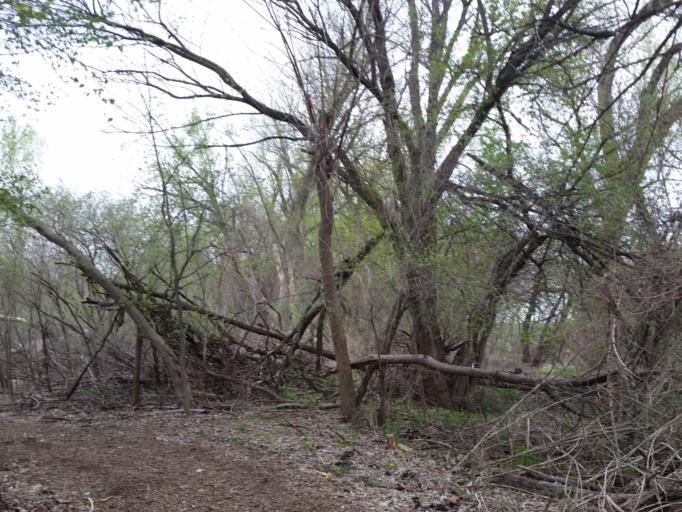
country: US
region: Nebraska
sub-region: Sarpy County
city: Bellevue
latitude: 41.1479
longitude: -95.8847
